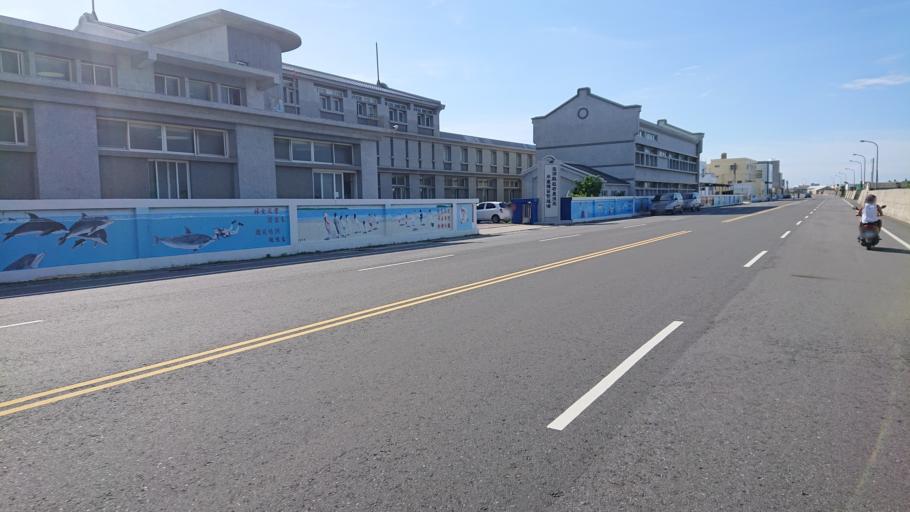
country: TW
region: Taiwan
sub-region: Penghu
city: Ma-kung
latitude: 23.5202
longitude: 119.5738
